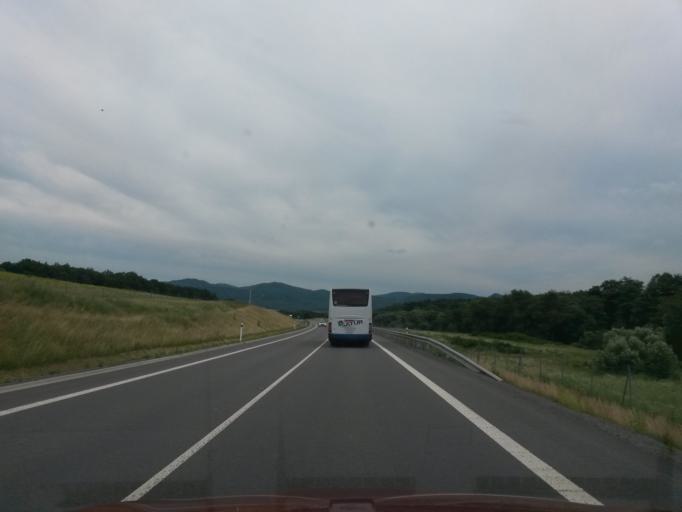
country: SK
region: Banskobystricky
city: Ziar nad Hronom
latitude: 48.5975
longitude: 18.8210
